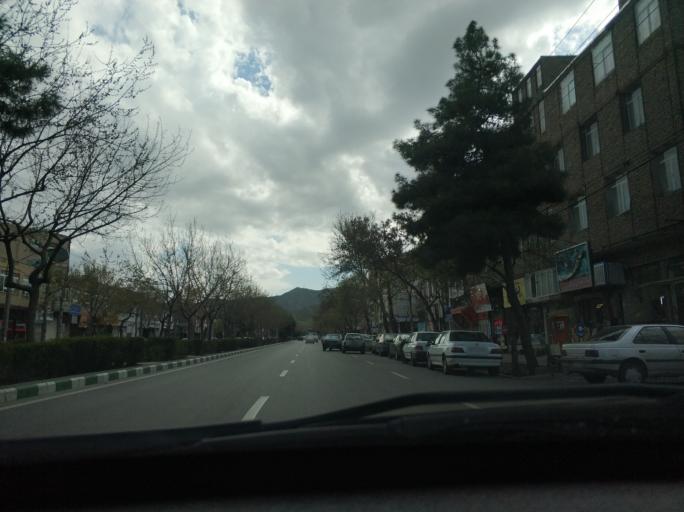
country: IR
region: Razavi Khorasan
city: Mashhad
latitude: 36.2701
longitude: 59.5888
